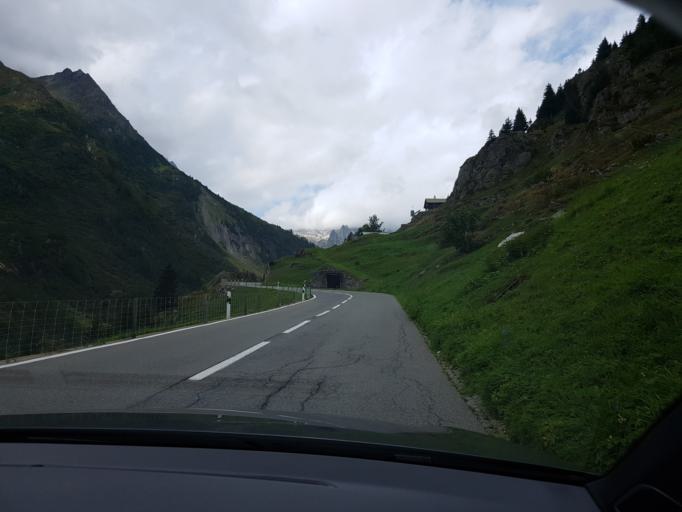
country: CH
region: Uri
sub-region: Uri
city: Andermatt
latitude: 46.7339
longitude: 8.5336
